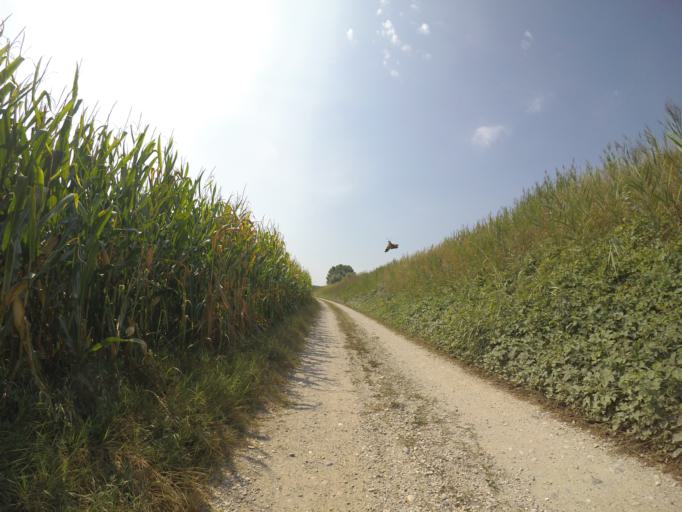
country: IT
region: Friuli Venezia Giulia
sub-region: Provincia di Udine
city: Pertegada
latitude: 45.7146
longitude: 13.0411
